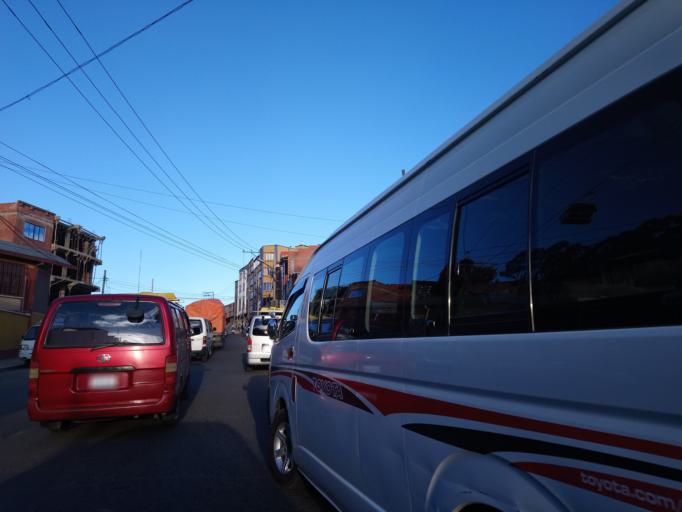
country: BO
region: La Paz
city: La Paz
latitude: -16.4871
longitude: -68.1321
